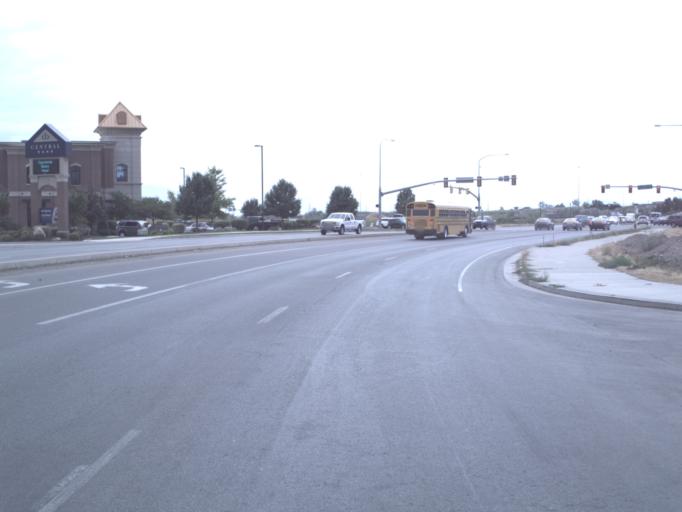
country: US
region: Utah
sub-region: Utah County
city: Pleasant Grove
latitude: 40.3552
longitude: -111.7636
